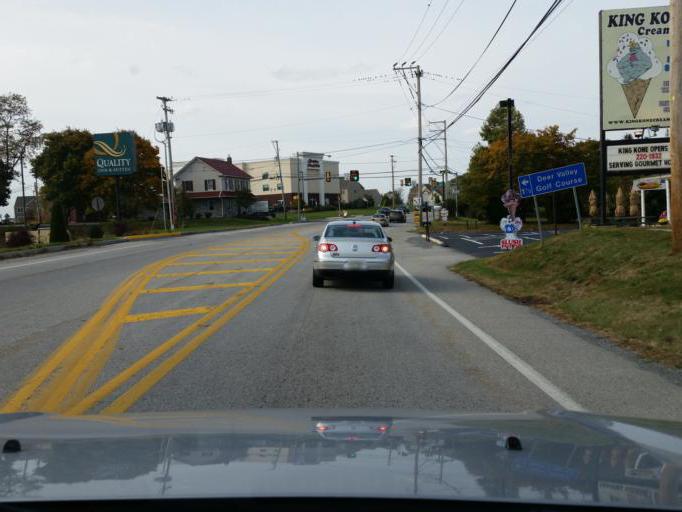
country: US
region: Pennsylvania
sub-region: Dauphin County
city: Hummelstown
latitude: 40.3002
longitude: -76.6903
